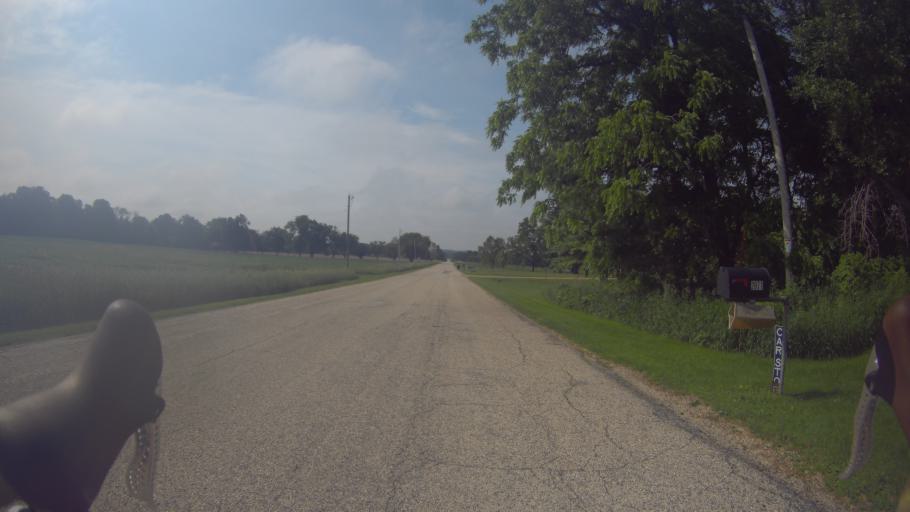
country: US
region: Wisconsin
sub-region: Dane County
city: Stoughton
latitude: 42.9612
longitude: -89.1810
